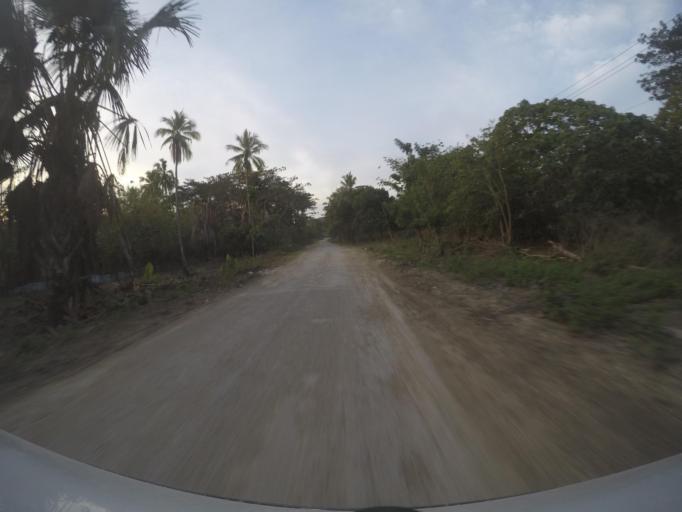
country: TL
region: Viqueque
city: Viqueque
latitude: -8.9205
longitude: 126.3973
